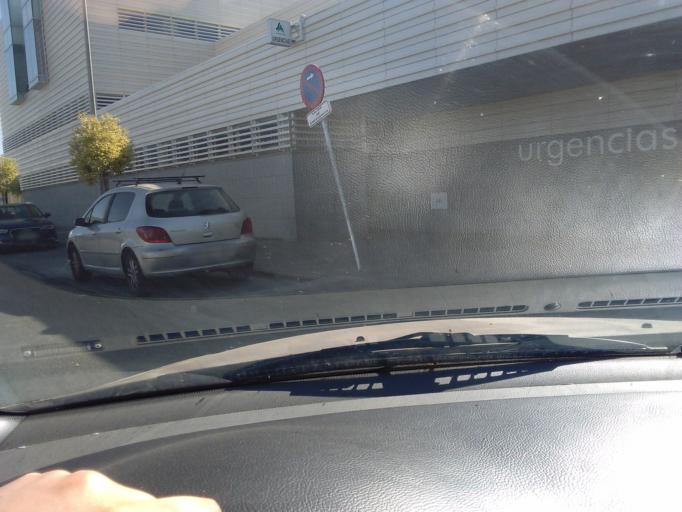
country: ES
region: Andalusia
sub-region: Provincia de Sevilla
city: Sevilla
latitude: 37.3875
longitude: -5.9141
